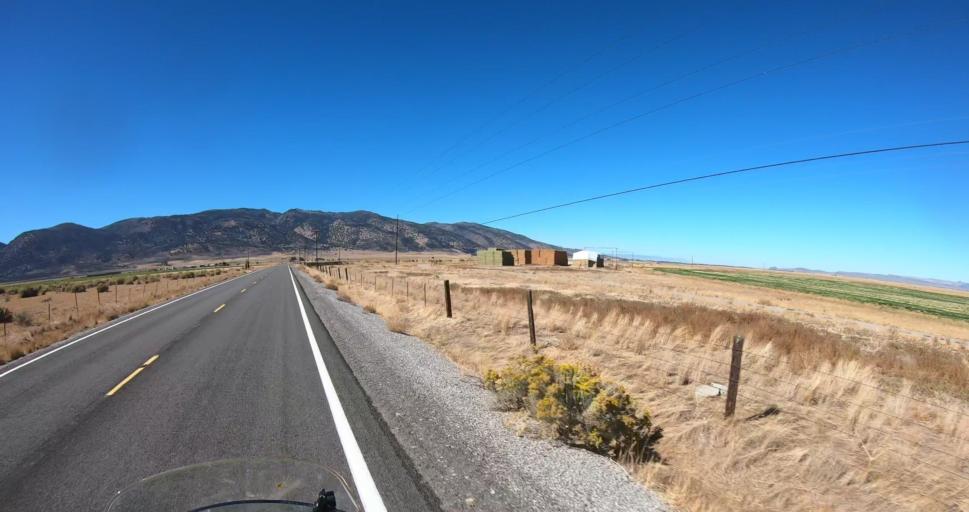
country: US
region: Oregon
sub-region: Lake County
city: Lakeview
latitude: 42.6146
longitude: -120.4725
